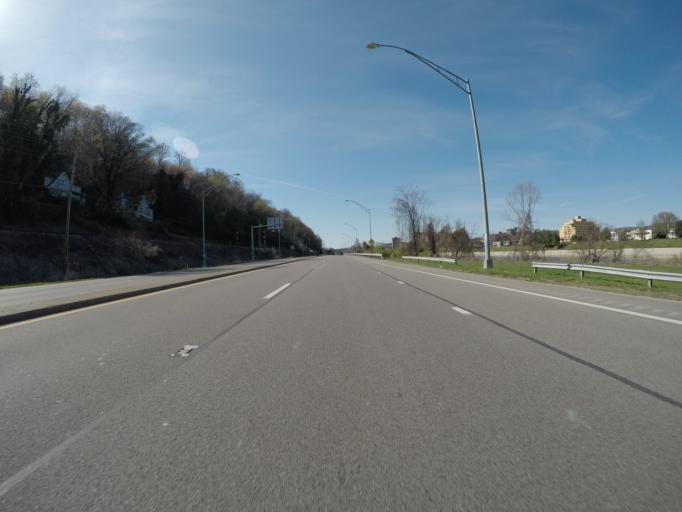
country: US
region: West Virginia
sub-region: Kanawha County
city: Charleston
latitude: 38.3400
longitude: -81.6313
